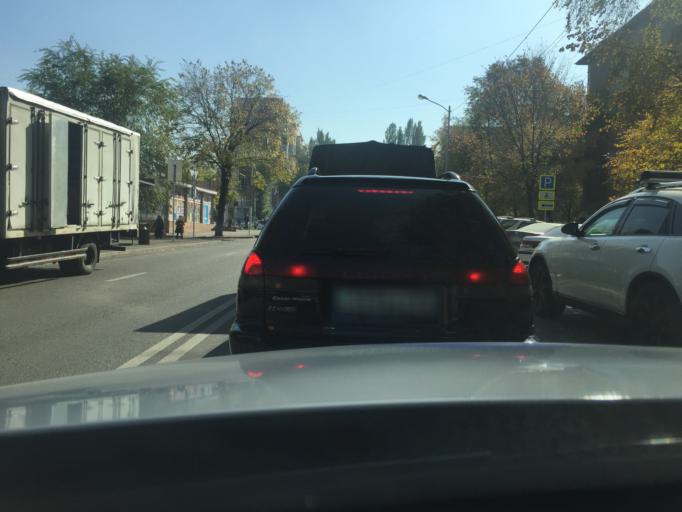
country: KZ
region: Almaty Qalasy
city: Almaty
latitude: 43.2533
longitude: 76.9114
